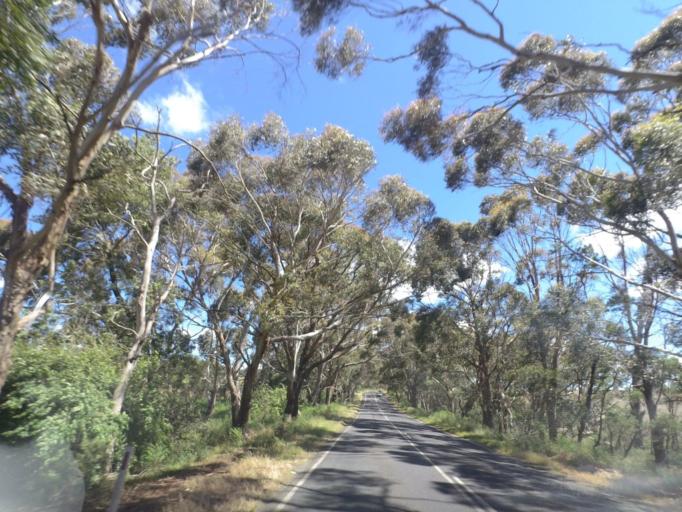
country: AU
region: Victoria
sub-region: Mount Alexander
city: Castlemaine
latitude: -37.3065
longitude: 144.4141
